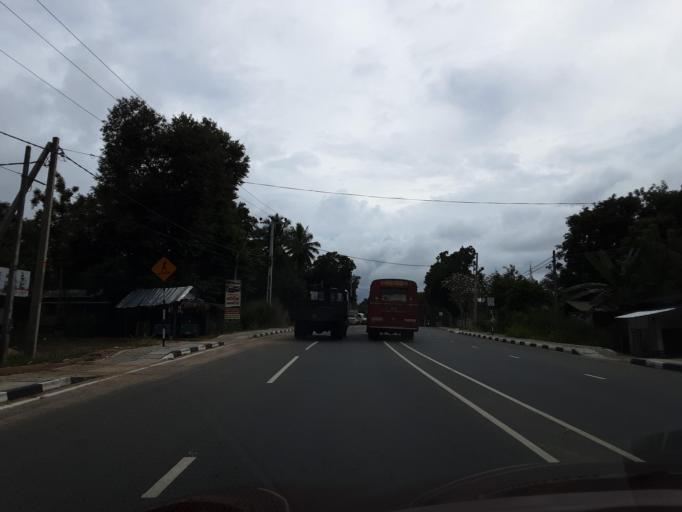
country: LK
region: Uva
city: Badulla
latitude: 7.3972
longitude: 81.2411
